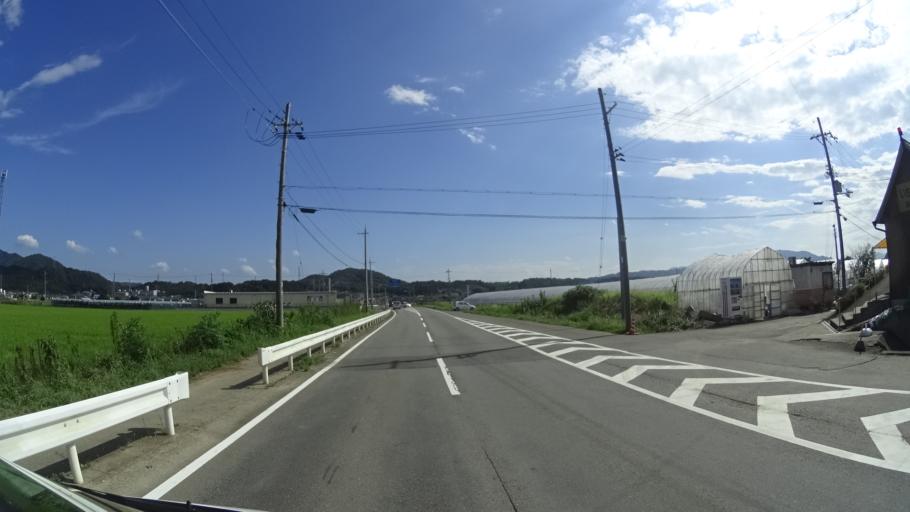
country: JP
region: Kyoto
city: Fukuchiyama
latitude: 35.3069
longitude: 135.1707
